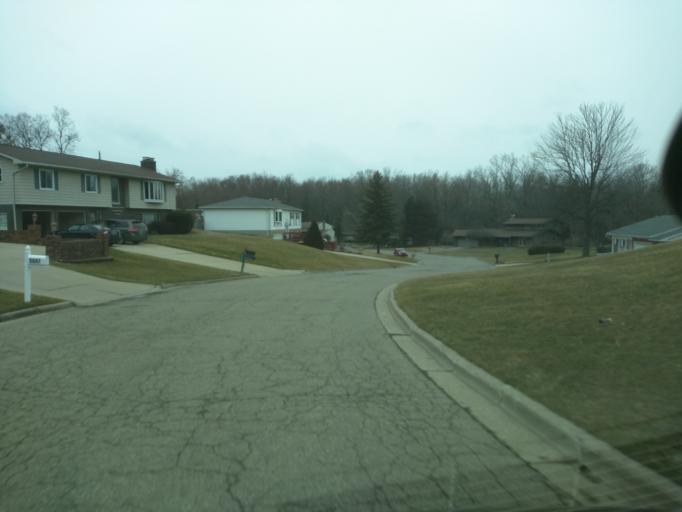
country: US
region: Michigan
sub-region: Eaton County
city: Waverly
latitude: 42.7570
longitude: -84.6212
